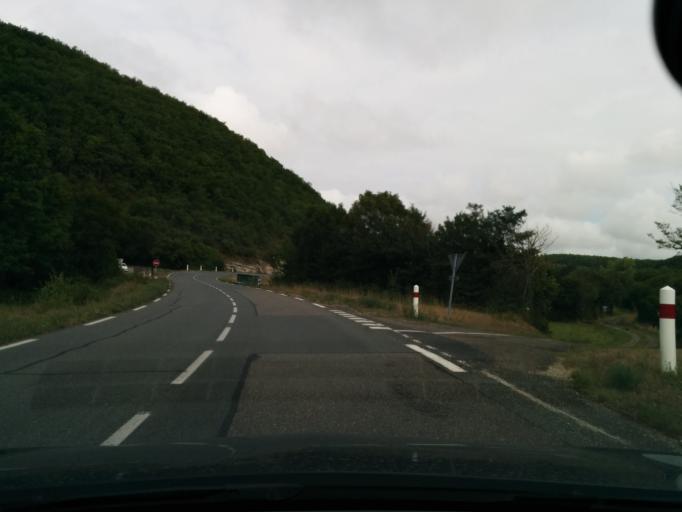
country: FR
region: Midi-Pyrenees
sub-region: Departement du Lot
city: Le Vigan
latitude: 44.6899
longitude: 1.4858
